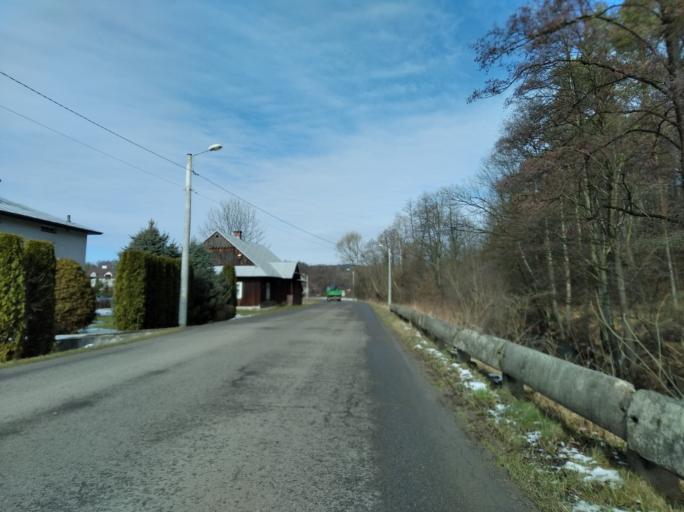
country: PL
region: Subcarpathian Voivodeship
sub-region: Powiat brzozowski
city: Jasienica Rosielna
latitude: 49.7514
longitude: 21.9147
